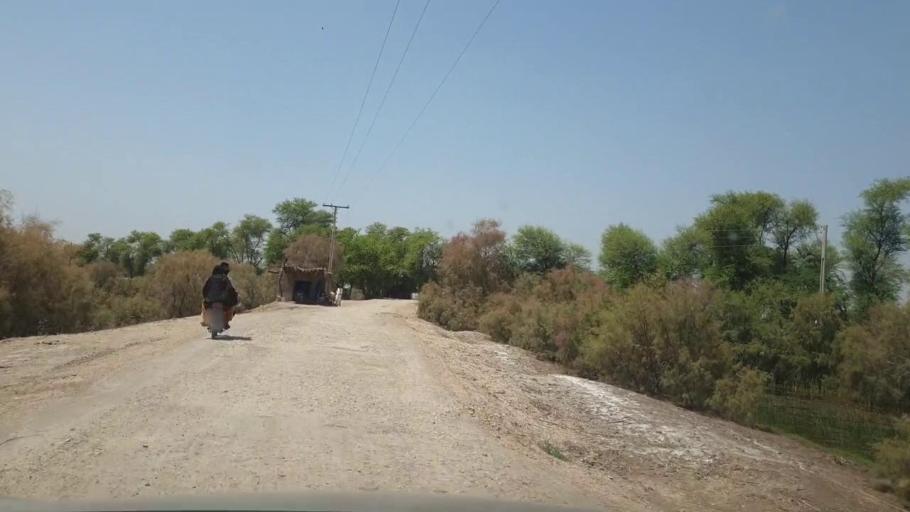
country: PK
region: Sindh
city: Warah
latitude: 27.4838
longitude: 67.7331
